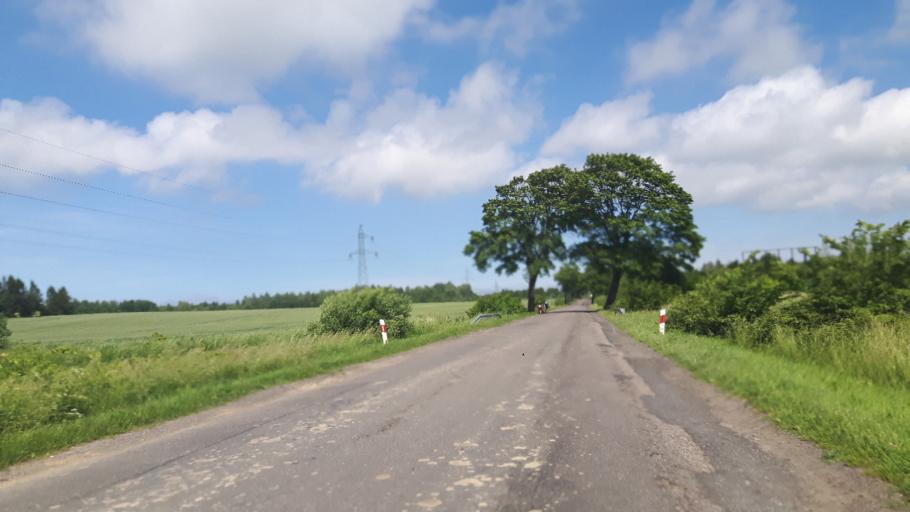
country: PL
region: Pomeranian Voivodeship
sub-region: Powiat slupski
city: Ustka
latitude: 54.5556
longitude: 16.8394
